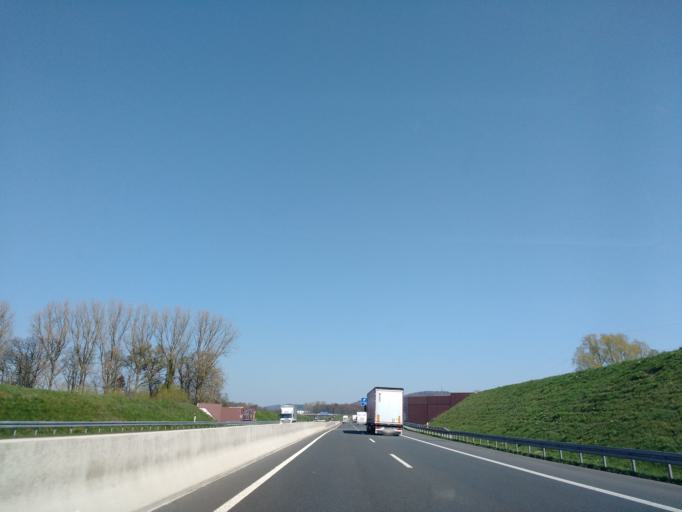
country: DE
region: North Rhine-Westphalia
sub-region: Regierungsbezirk Detmold
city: Steinhagen
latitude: 51.9966
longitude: 8.4428
